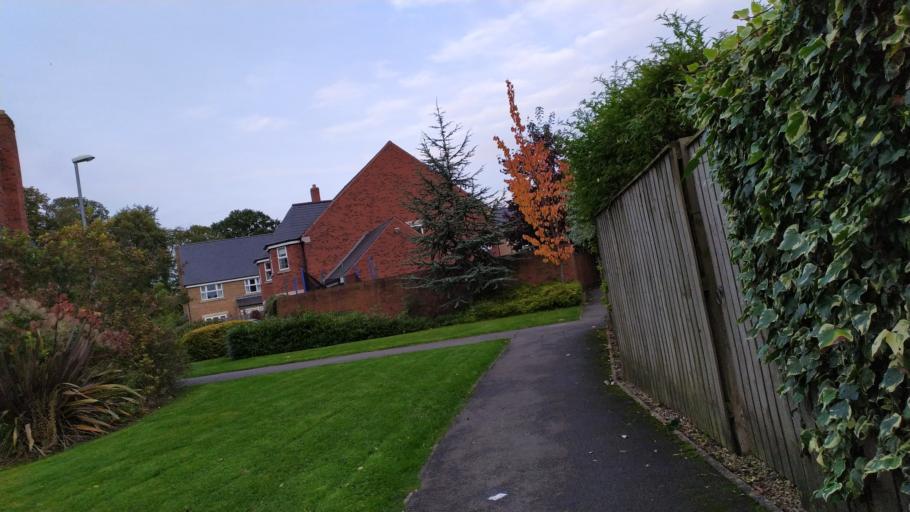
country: GB
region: England
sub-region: City and Borough of Leeds
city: Horsforth
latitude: 53.8309
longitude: -1.5905
